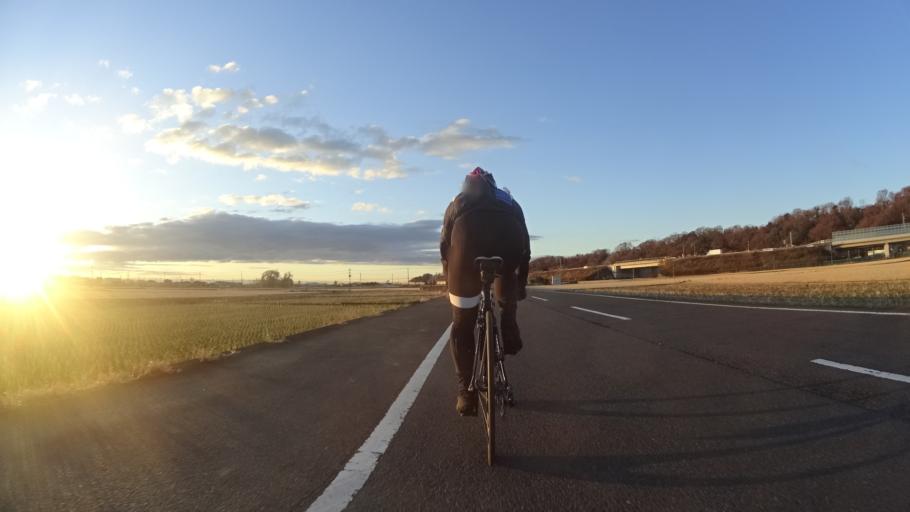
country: JP
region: Kanagawa
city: Zama
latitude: 35.5091
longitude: 139.3674
